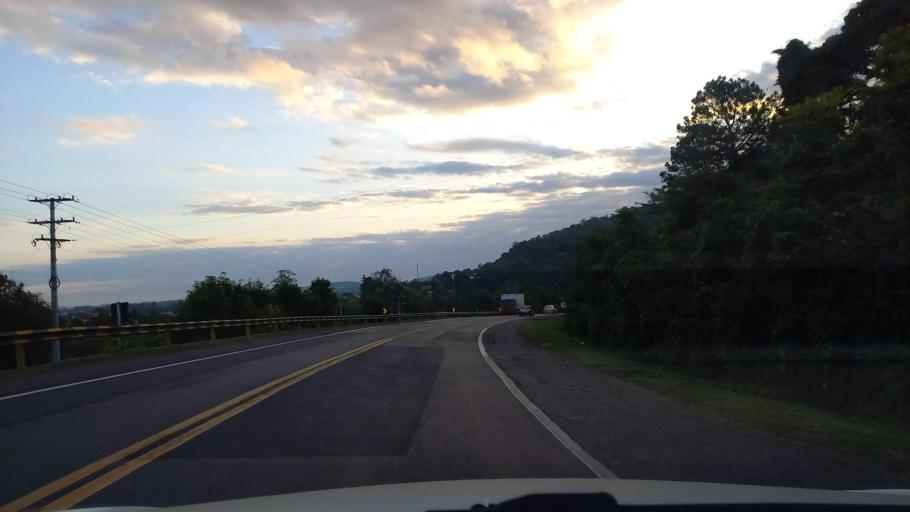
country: BR
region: Rio Grande do Sul
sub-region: Santa Cruz Do Sul
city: Santa Cruz do Sul
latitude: -29.6849
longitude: -52.4387
